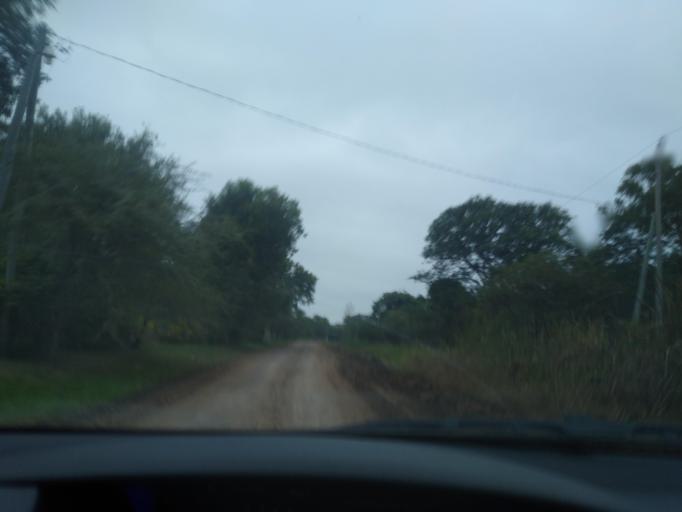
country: AR
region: Chaco
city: Colonia Benitez
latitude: -27.3314
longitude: -58.9643
